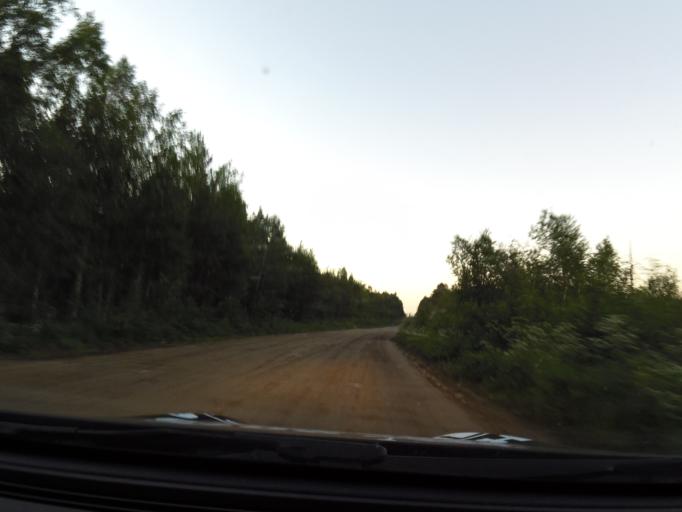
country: RU
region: Leningrad
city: Voznesen'ye
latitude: 60.8585
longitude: 35.9343
